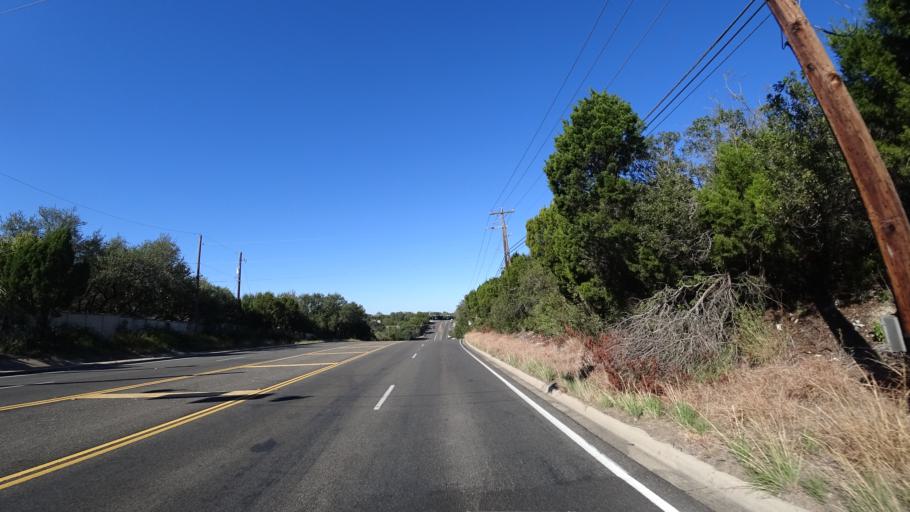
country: US
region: Texas
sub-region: Travis County
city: West Lake Hills
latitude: 30.3413
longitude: -97.7750
